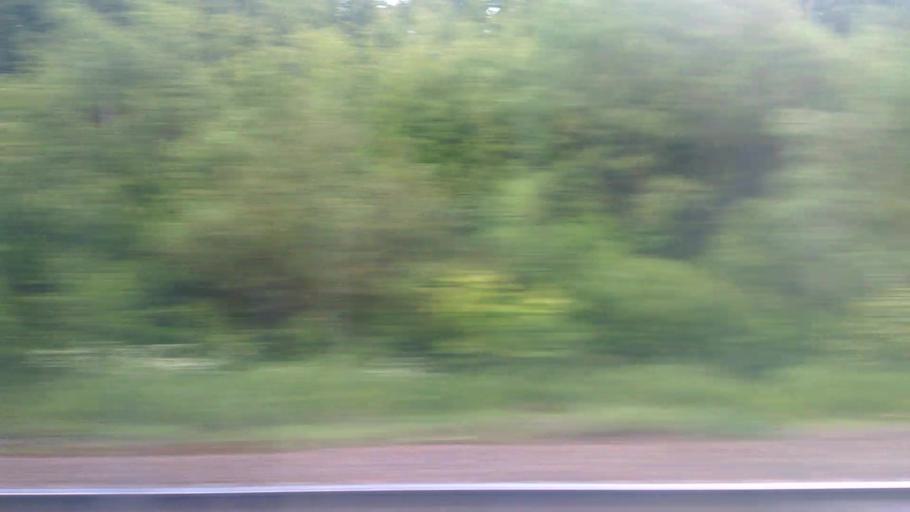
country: RU
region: Moskovskaya
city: Zhilevo
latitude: 55.0650
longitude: 37.9866
